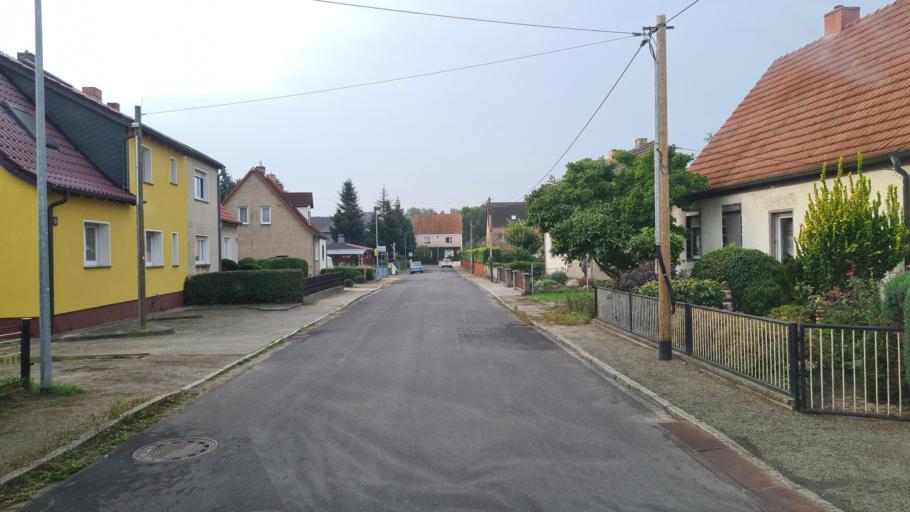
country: DE
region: Brandenburg
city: Lauchhammer
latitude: 51.4936
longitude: 13.7720
